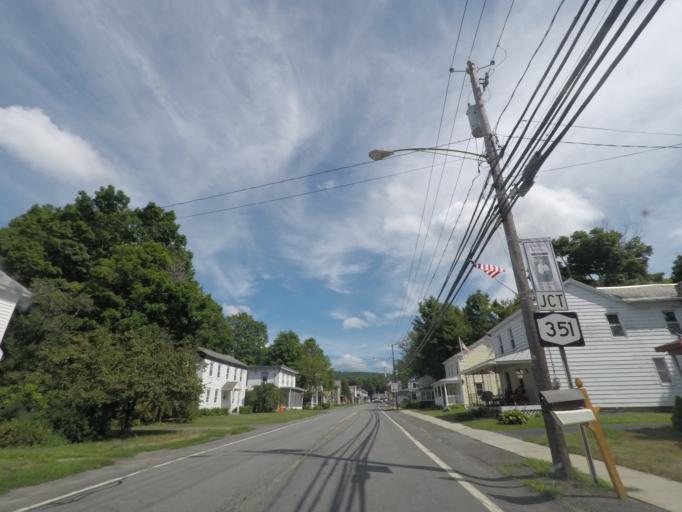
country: US
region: New York
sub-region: Rensselaer County
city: Poestenkill
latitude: 42.6916
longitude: -73.5666
